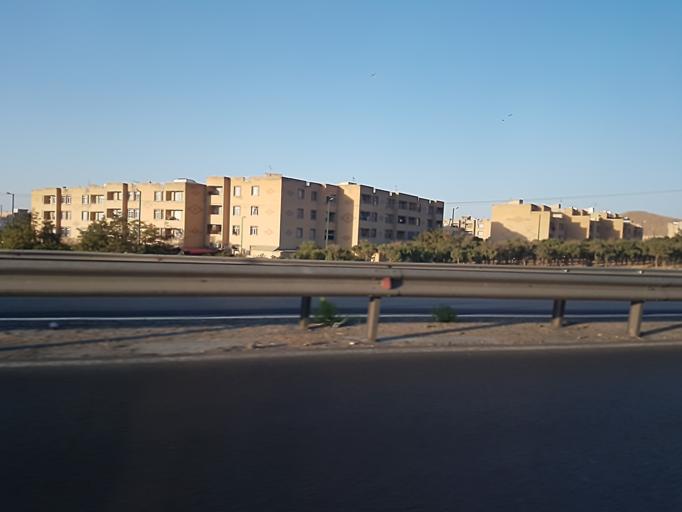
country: IR
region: Markazi
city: Arak
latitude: 34.0681
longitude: 49.7168
